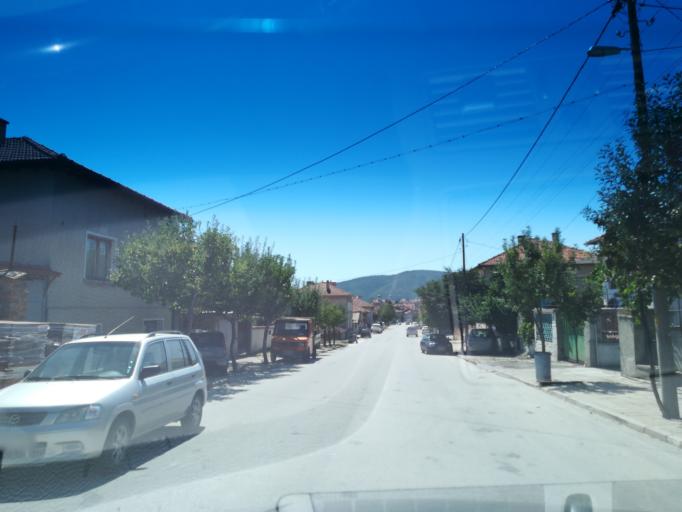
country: BG
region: Pazardzhik
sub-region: Obshtina Strelcha
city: Strelcha
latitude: 42.5144
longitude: 24.3214
